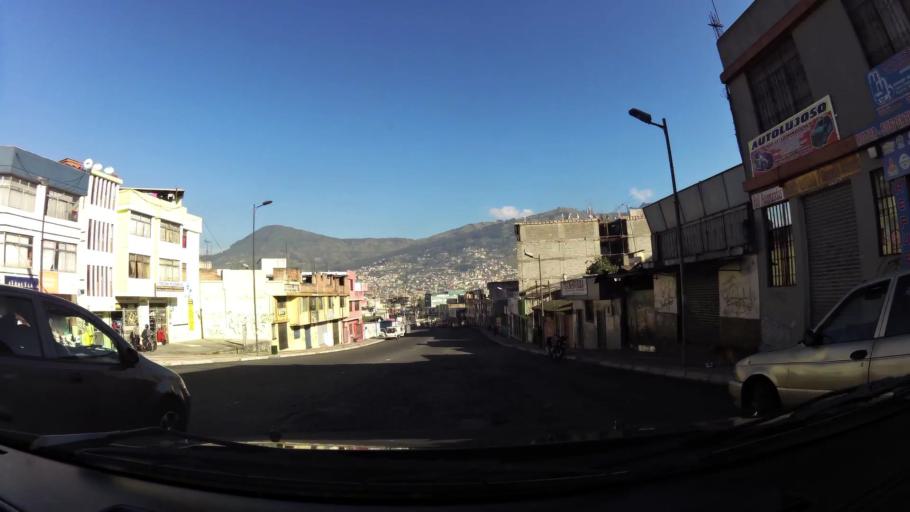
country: EC
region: Pichincha
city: Quito
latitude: -0.2453
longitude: -78.5168
